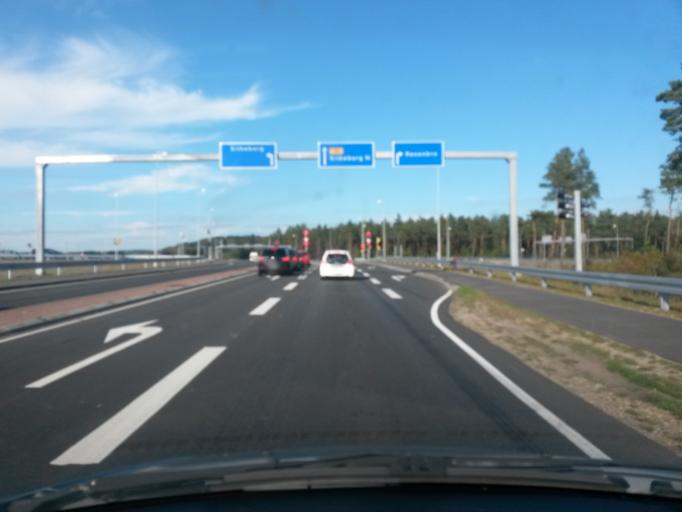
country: DK
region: Central Jutland
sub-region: Silkeborg Kommune
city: Svejbaek
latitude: 56.1689
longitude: 9.6043
